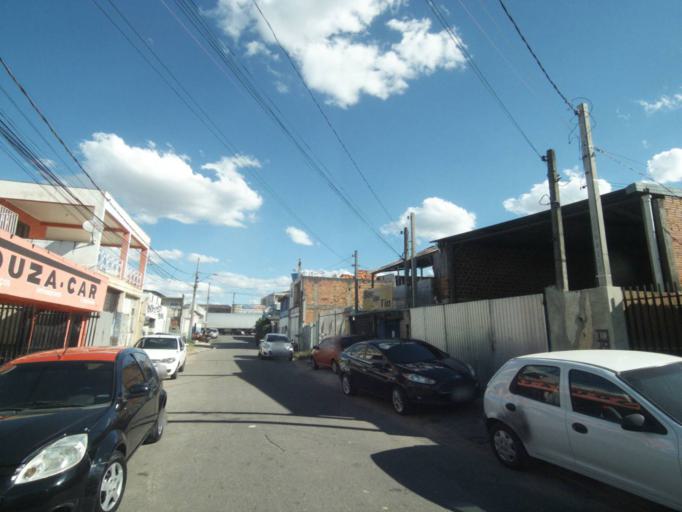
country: BR
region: Parana
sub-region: Curitiba
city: Curitiba
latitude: -25.5133
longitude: -49.3363
